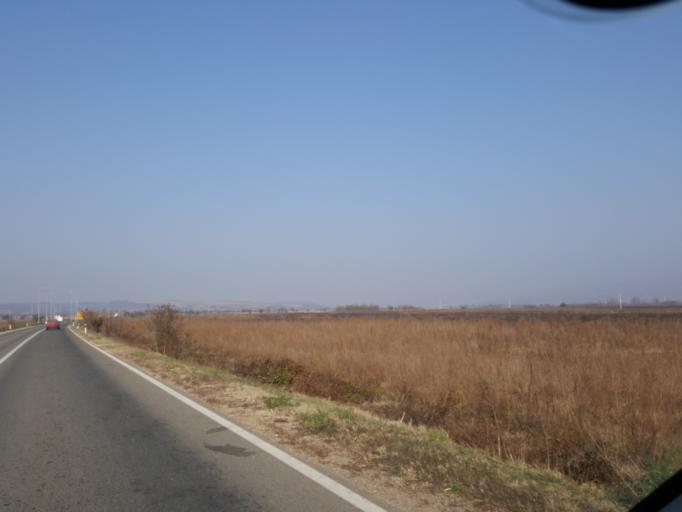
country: RS
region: Central Serbia
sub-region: Jablanicki Okrug
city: Leskovac
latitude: 43.0235
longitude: 21.9475
